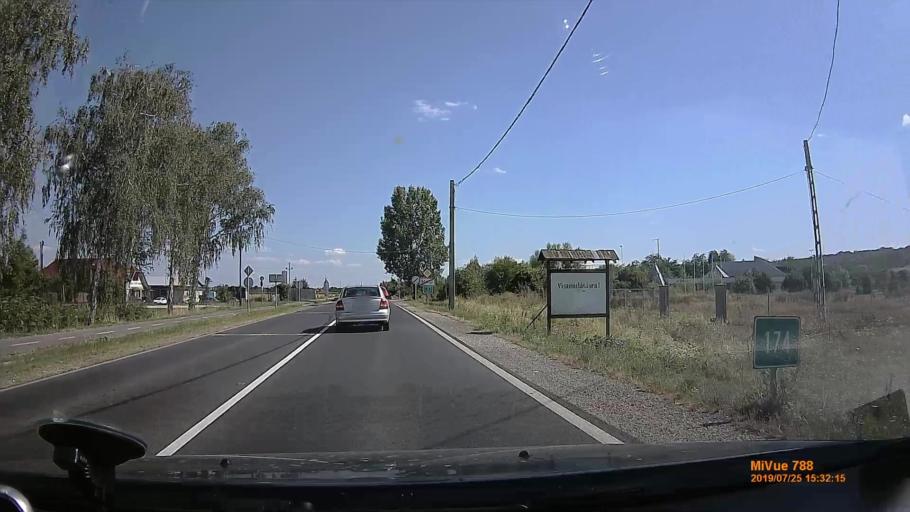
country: HU
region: Borsod-Abauj-Zemplen
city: Malyi
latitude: 48.0079
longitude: 20.8274
